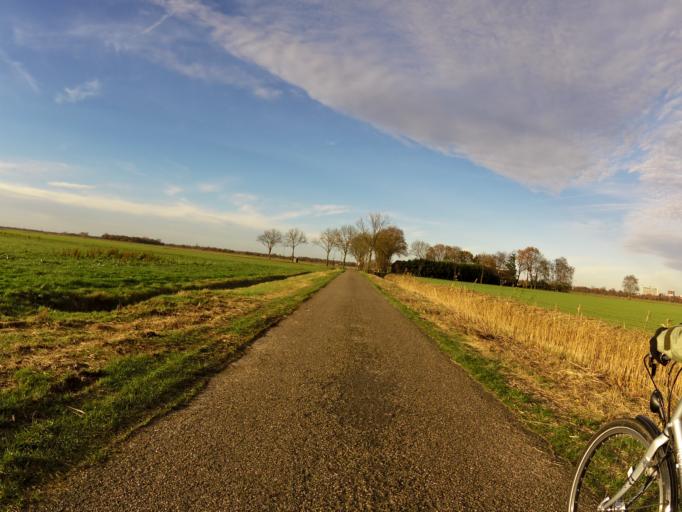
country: NL
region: North Brabant
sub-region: Gemeente Vught
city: Vught
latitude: 51.6701
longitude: 5.2718
